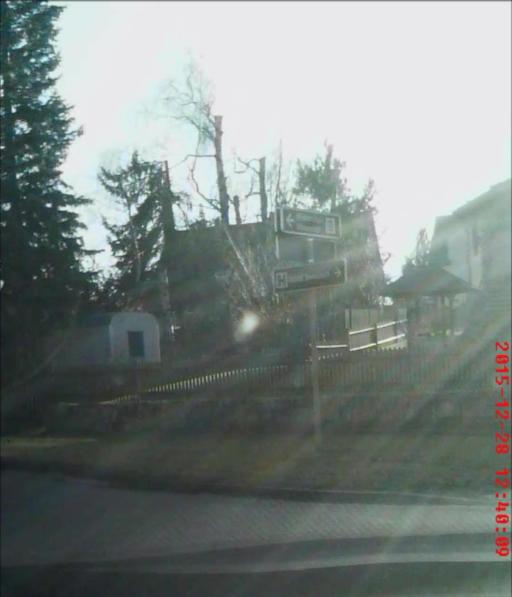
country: DE
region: Thuringia
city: Ossmanstedt
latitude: 51.0111
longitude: 11.4234
